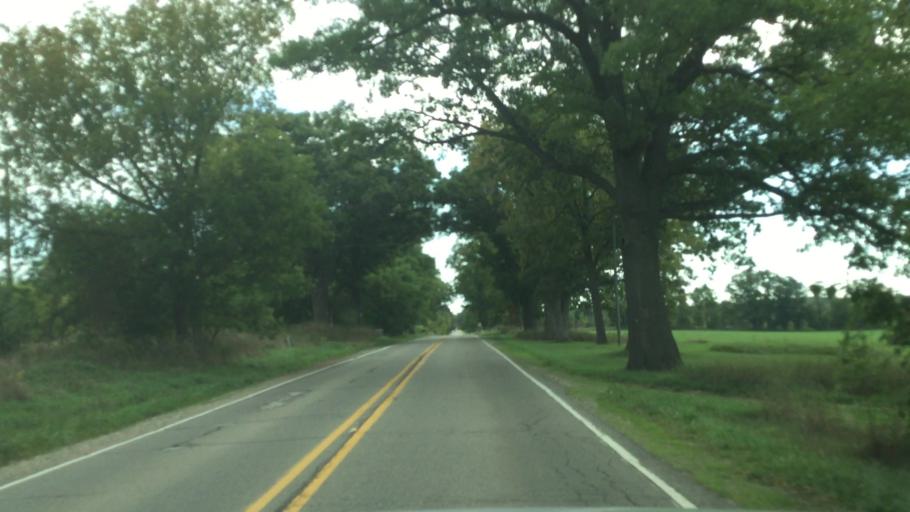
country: US
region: Michigan
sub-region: Genesee County
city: Argentine
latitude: 42.7047
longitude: -83.8546
